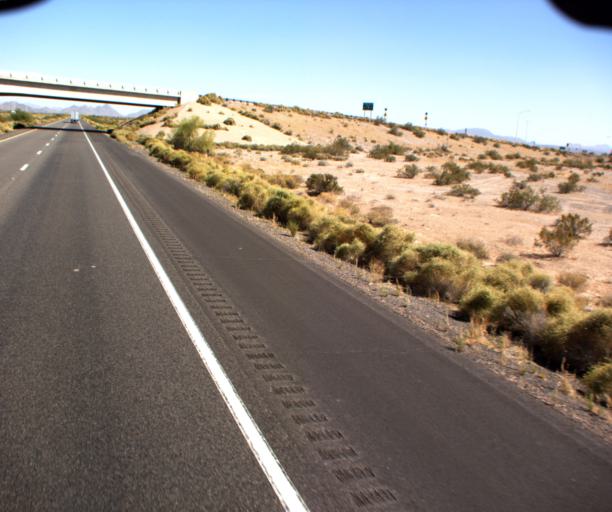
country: US
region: Arizona
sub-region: Maricopa County
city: Gila Bend
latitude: 32.9254
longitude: -112.6725
